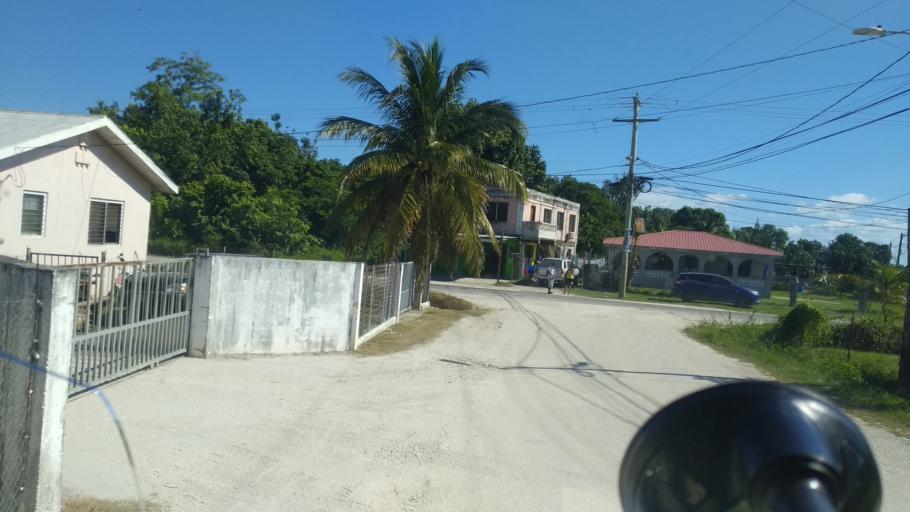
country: BZ
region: Belize
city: Belize City
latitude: 17.5568
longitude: -88.3027
